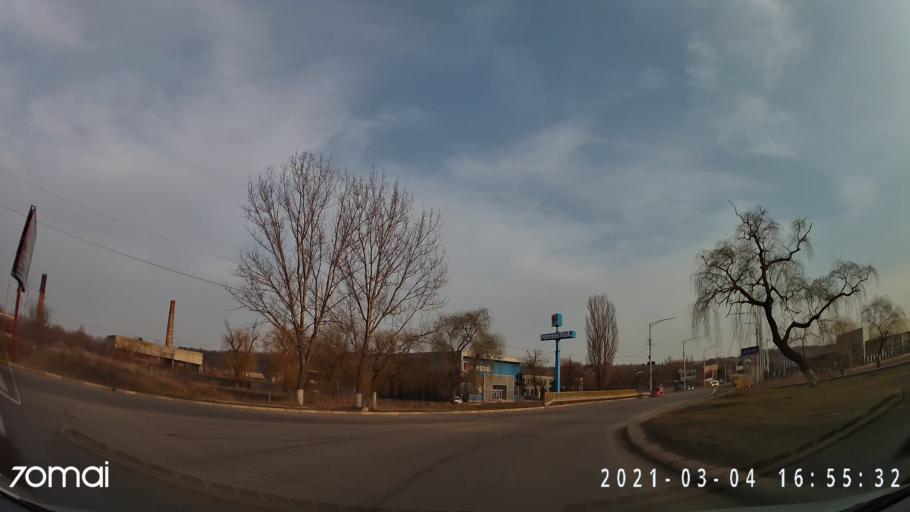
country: MD
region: Balti
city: Balti
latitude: 47.7556
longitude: 27.9415
